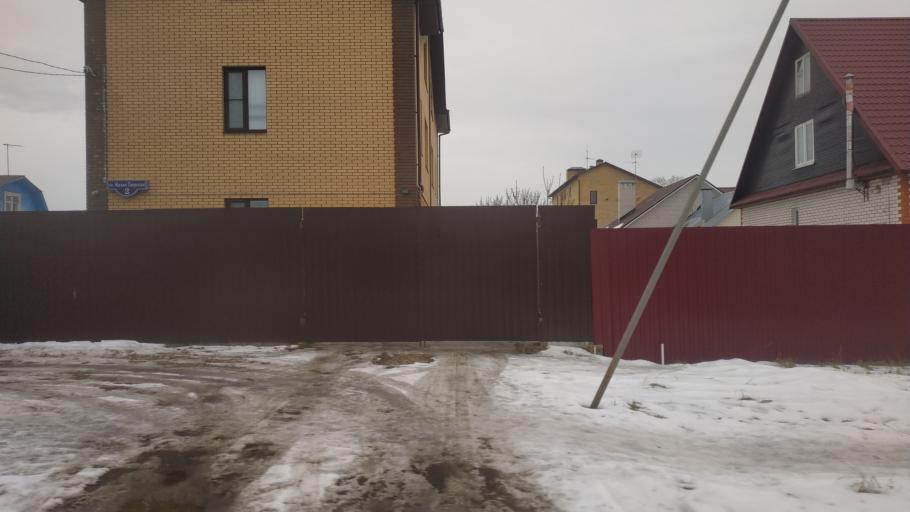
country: RU
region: Tverskaya
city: Tver
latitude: 56.8856
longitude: 35.8965
